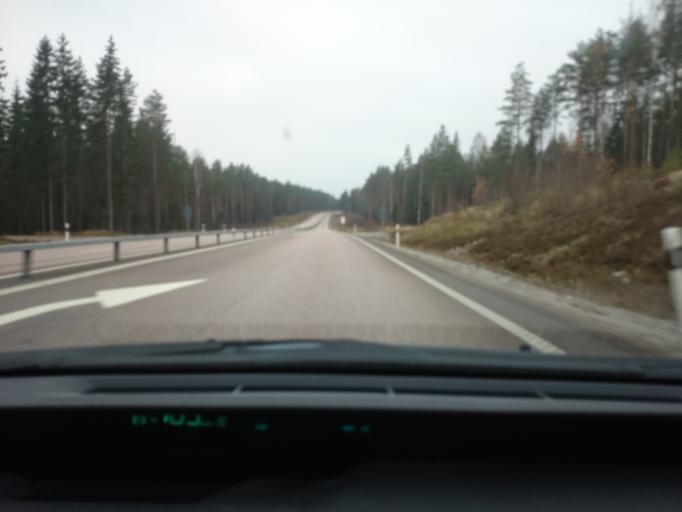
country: SE
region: Vaestmanland
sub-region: Sala Kommun
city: Sala
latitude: 60.0116
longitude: 16.3857
